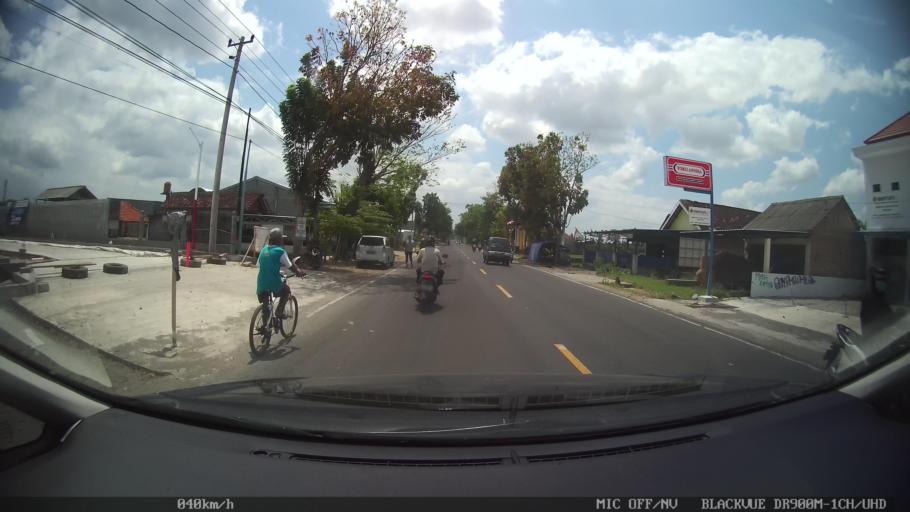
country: ID
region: Daerah Istimewa Yogyakarta
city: Bantul
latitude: -7.9023
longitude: 110.3457
